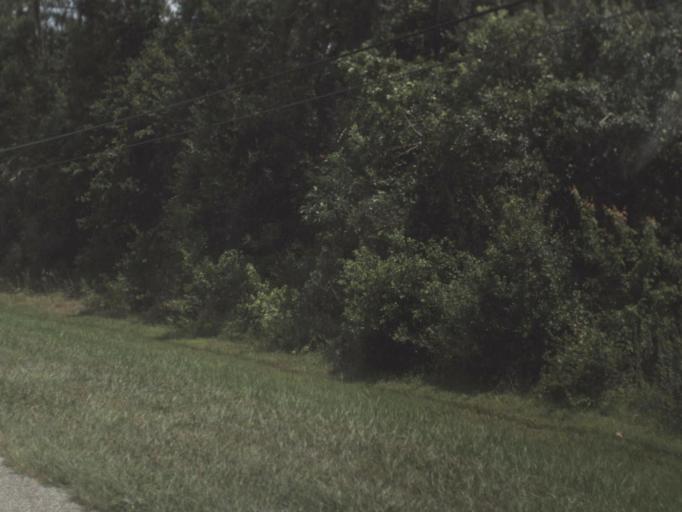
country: US
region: Florida
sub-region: Hillsborough County
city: Sun City Center
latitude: 27.7542
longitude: -82.3351
